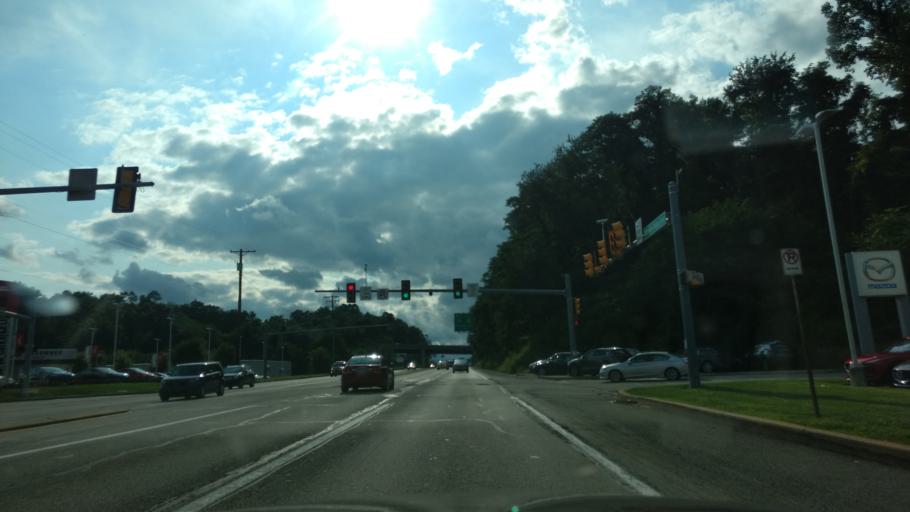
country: US
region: Pennsylvania
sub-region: Allegheny County
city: Monroeville
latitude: 40.4388
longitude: -79.7470
